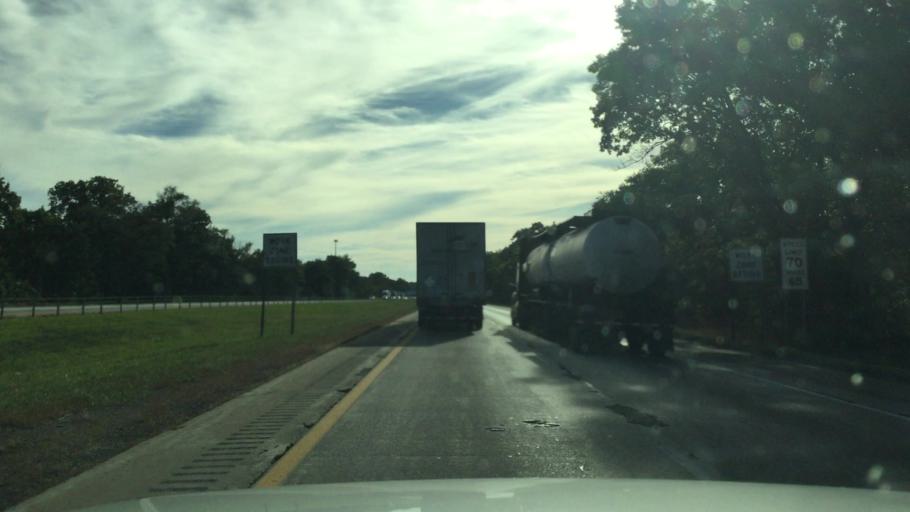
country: US
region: Michigan
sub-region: Calhoun County
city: Battle Creek
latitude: 42.2770
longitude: -85.1639
